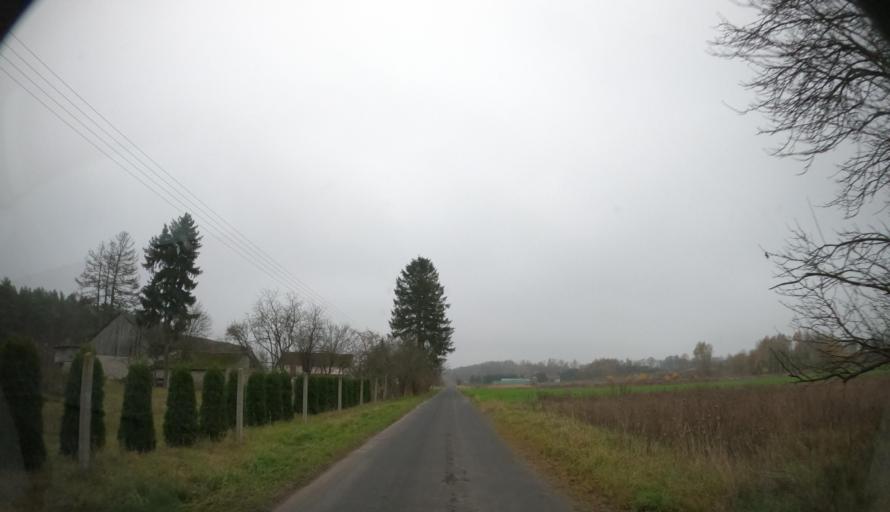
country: PL
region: West Pomeranian Voivodeship
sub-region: Powiat lobeski
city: Radowo Male
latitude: 53.6795
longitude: 15.4673
